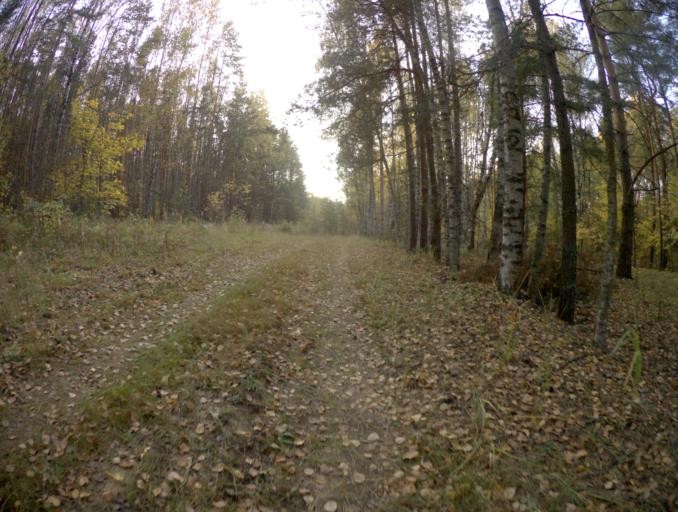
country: RU
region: Vladimir
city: Raduzhnyy
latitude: 56.0233
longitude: 40.2830
